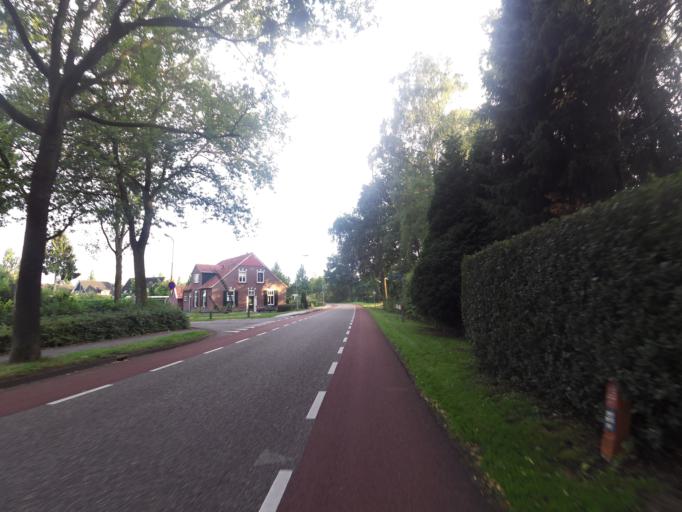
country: NL
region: Gelderland
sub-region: Oude IJsselstreek
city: Varsseveld
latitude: 51.8932
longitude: 6.4934
